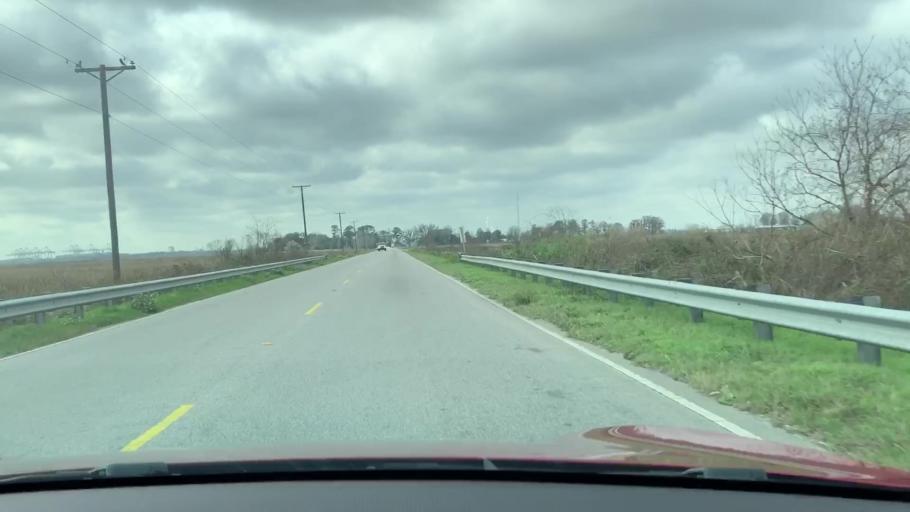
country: US
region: Georgia
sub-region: Chatham County
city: Port Wentworth
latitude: 32.1690
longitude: -81.1078
